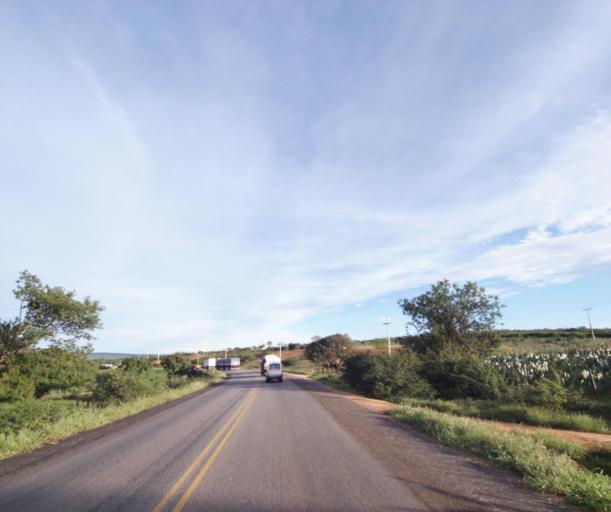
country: BR
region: Bahia
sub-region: Cacule
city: Cacule
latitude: -14.1997
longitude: -42.1350
